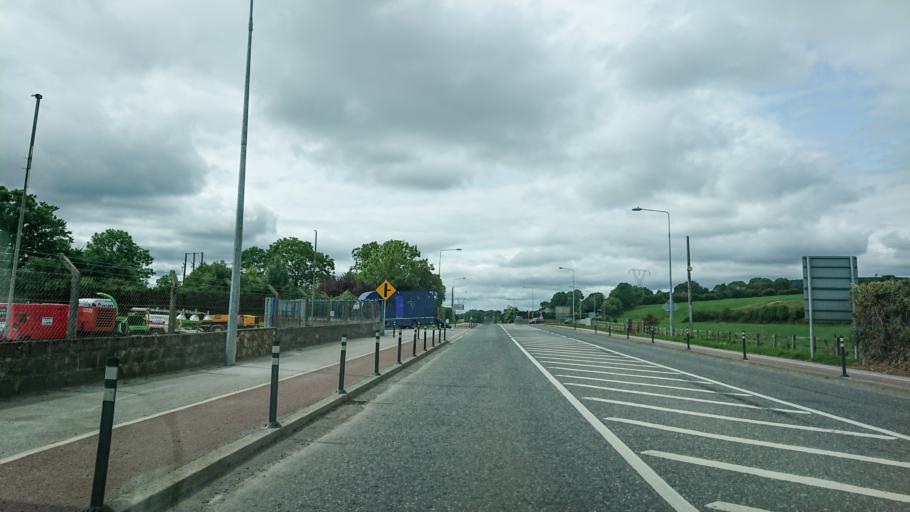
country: IE
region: Munster
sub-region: Waterford
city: Dungarvan
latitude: 52.1090
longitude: -7.6701
